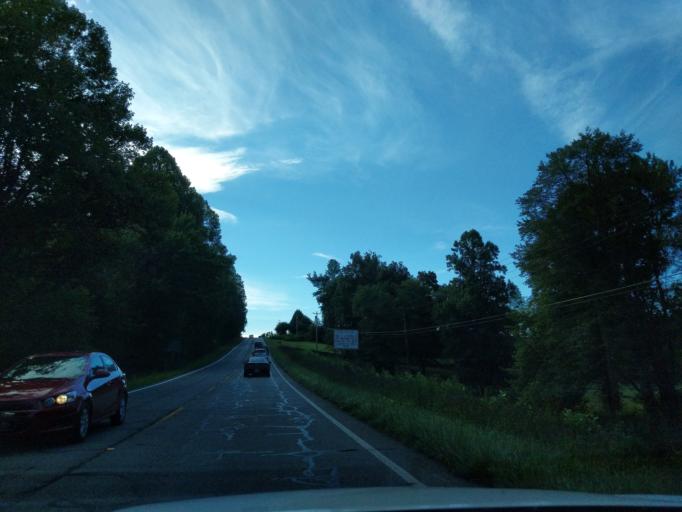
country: US
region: Georgia
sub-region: Fannin County
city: Blue Ridge
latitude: 34.8903
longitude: -84.3471
